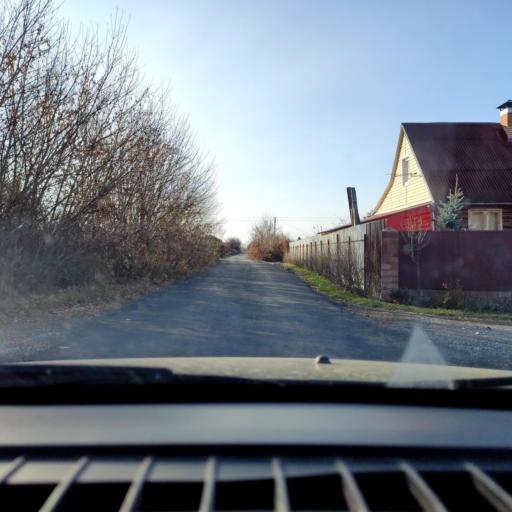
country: RU
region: Samara
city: Tol'yatti
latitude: 53.6644
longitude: 49.3418
